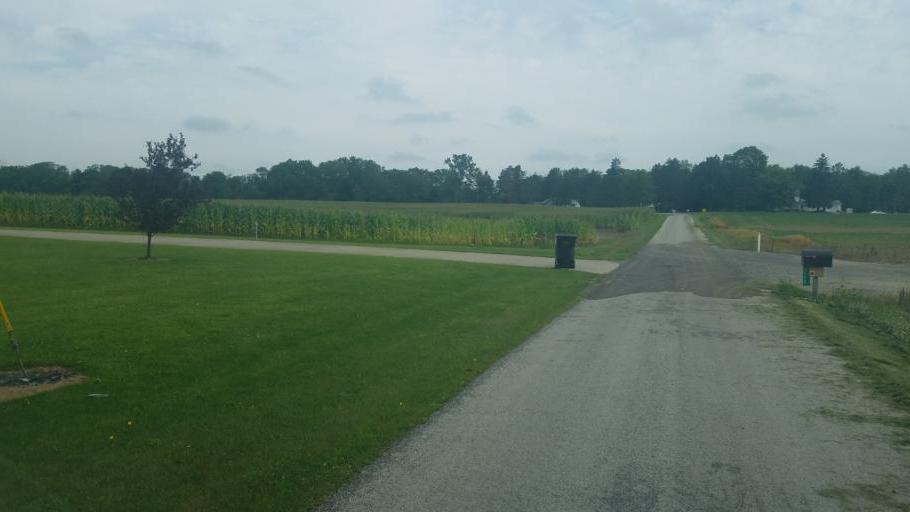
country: US
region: Ohio
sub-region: Morrow County
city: Cardington
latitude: 40.5100
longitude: -82.9391
